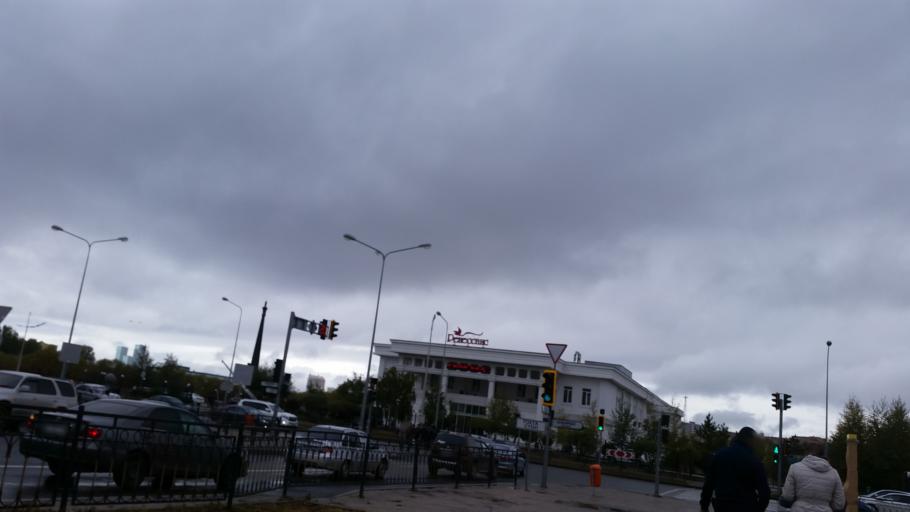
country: KZ
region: Astana Qalasy
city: Astana
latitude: 51.1521
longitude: 71.4614
